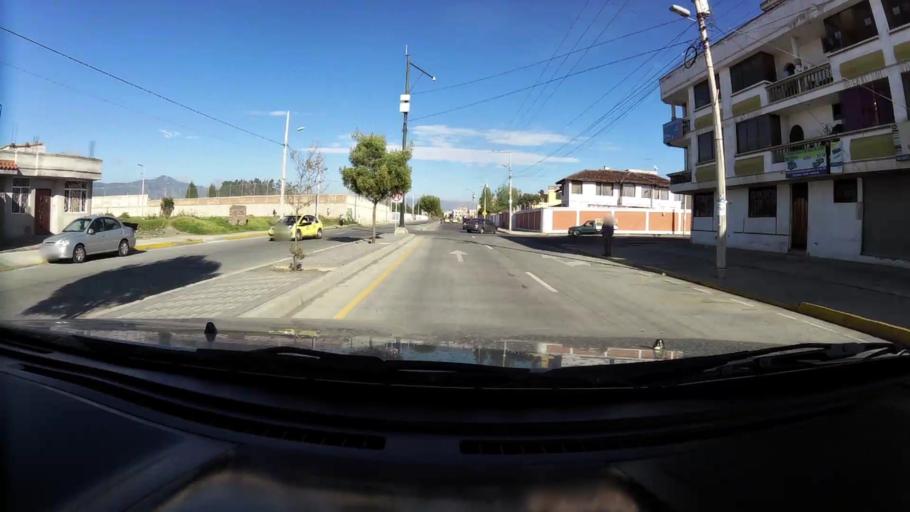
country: EC
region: Chimborazo
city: Riobamba
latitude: -1.6883
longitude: -78.6392
